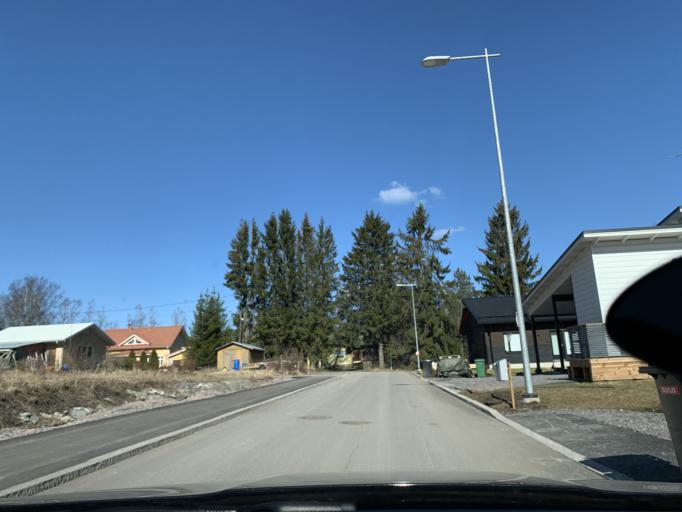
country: FI
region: Uusimaa
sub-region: Helsinki
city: Espoo
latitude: 60.1800
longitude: 24.5900
